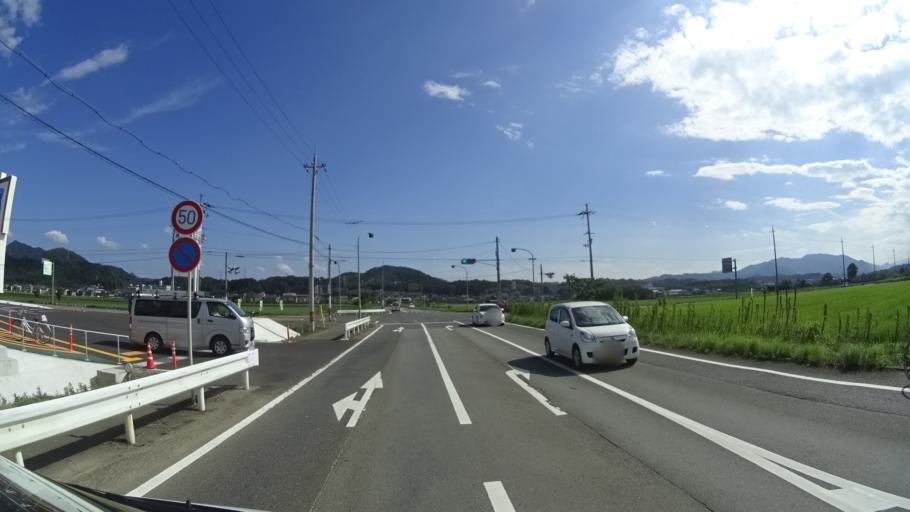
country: JP
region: Kyoto
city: Fukuchiyama
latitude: 35.3058
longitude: 135.1705
